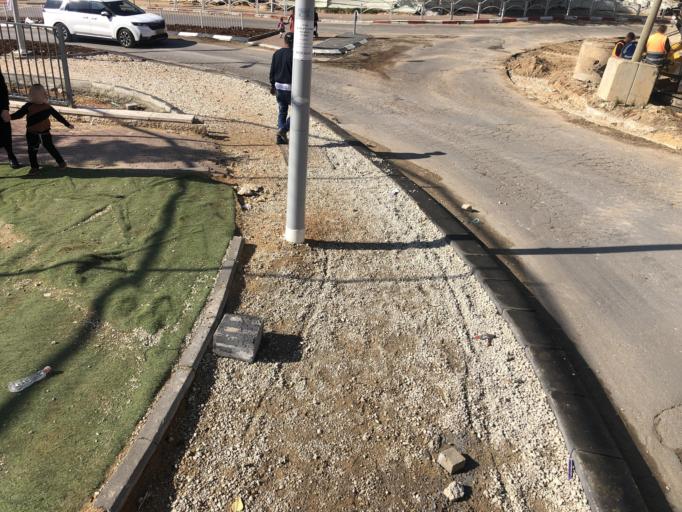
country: IL
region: Jerusalem
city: Modiin Ilit
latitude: 31.9290
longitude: 35.0460
